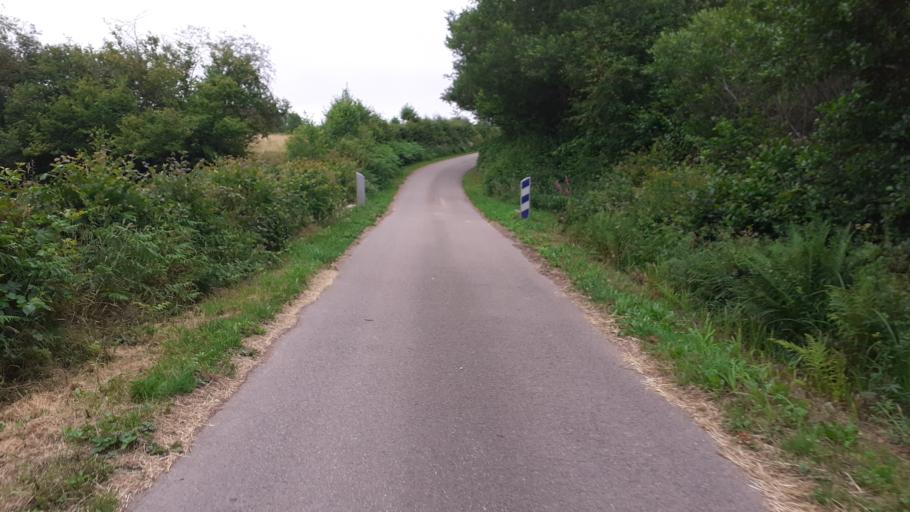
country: FR
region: Bourgogne
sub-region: Departement de la Cote-d'Or
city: Saulieu
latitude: 47.2725
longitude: 4.1334
